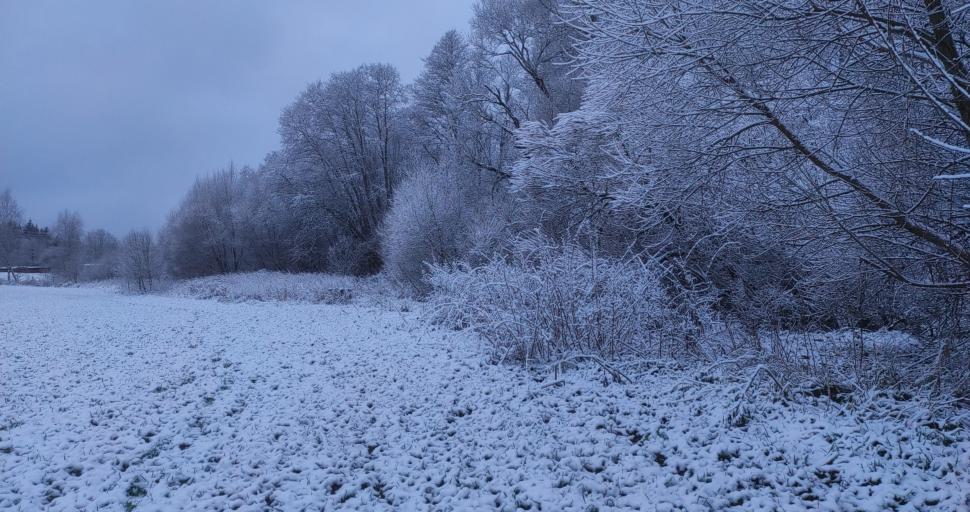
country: LV
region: Skrunda
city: Skrunda
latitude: 56.8736
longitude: 22.2282
